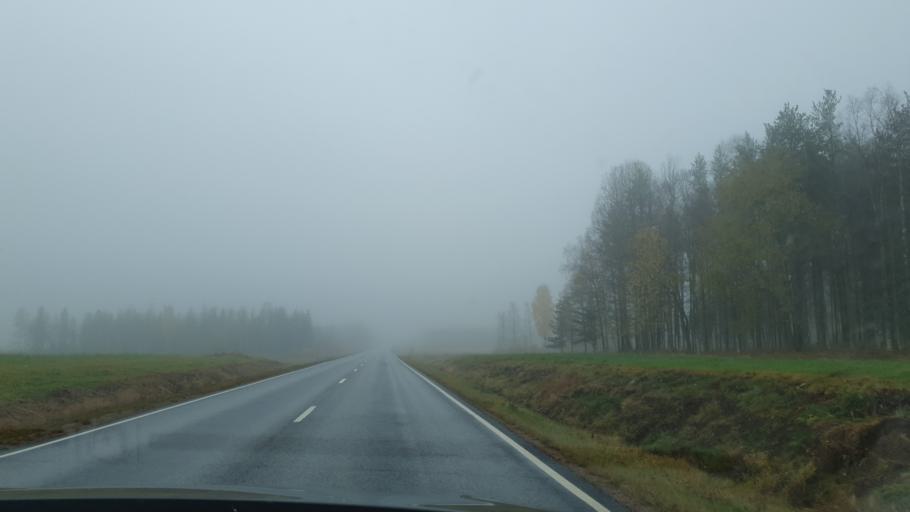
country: FI
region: Lapland
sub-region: Rovaniemi
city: Rovaniemi
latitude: 66.8001
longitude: 25.4141
